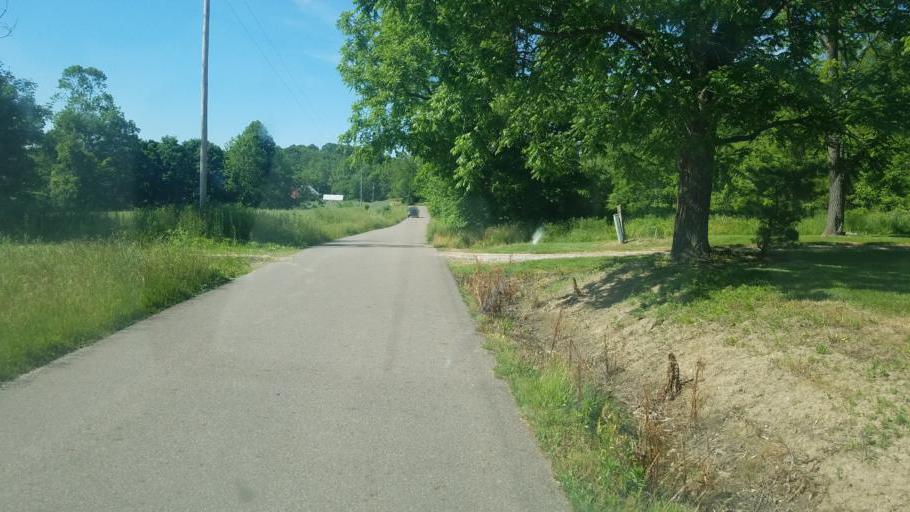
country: US
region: Ohio
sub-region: Tuscarawas County
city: Newcomerstown
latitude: 40.2256
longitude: -81.6707
